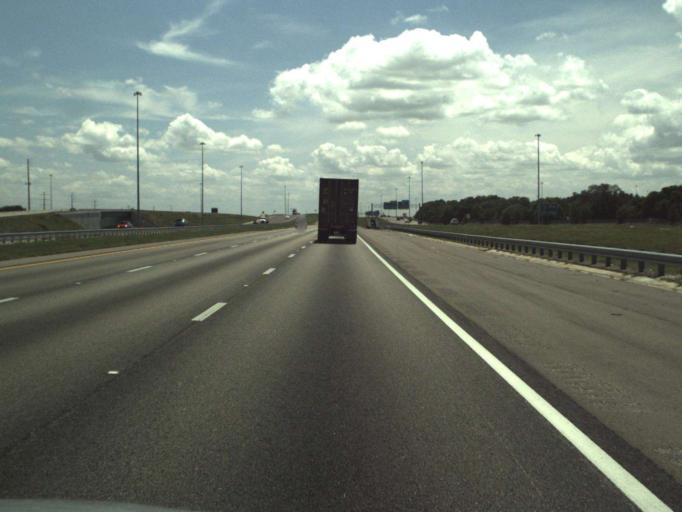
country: US
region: Florida
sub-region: Seminole County
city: Heathrow
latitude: 28.8031
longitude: -81.3423
